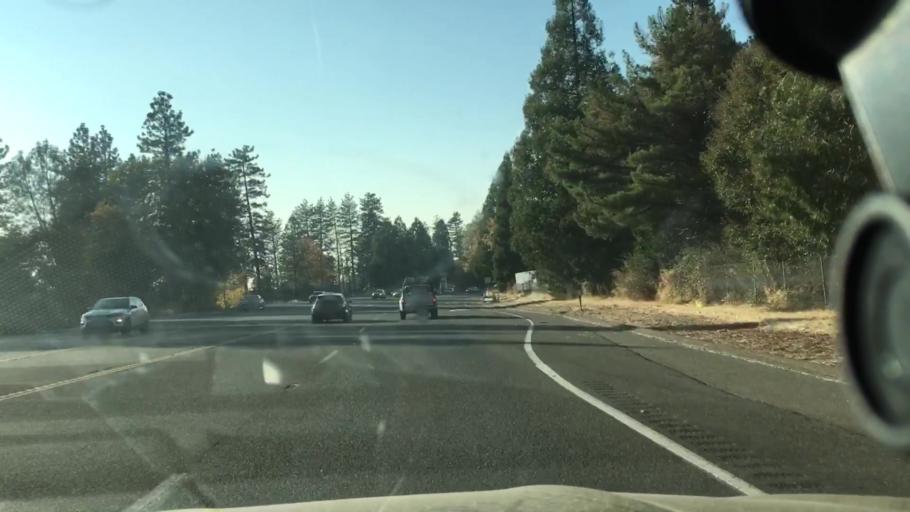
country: US
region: California
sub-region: El Dorado County
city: Camino
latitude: 38.7371
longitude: -120.7148
